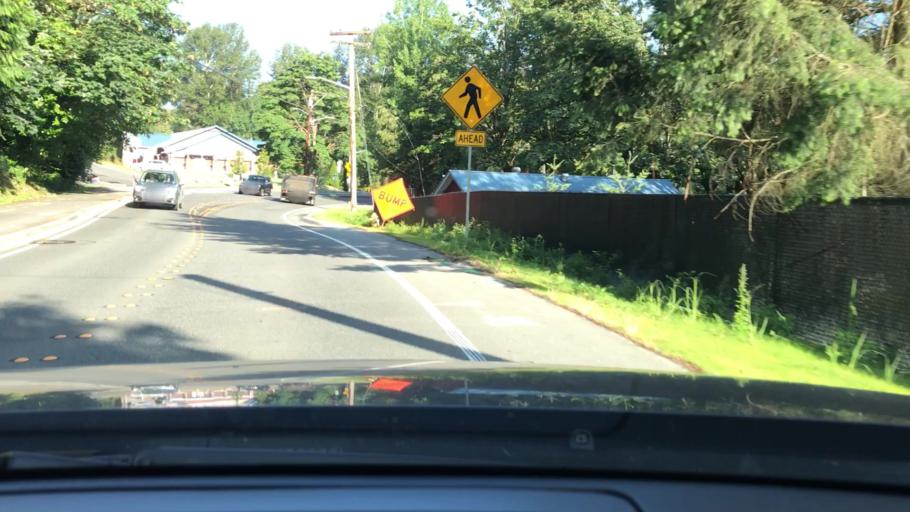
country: US
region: Washington
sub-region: King County
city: West Lake Sammamish
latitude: 47.5764
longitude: -122.1120
